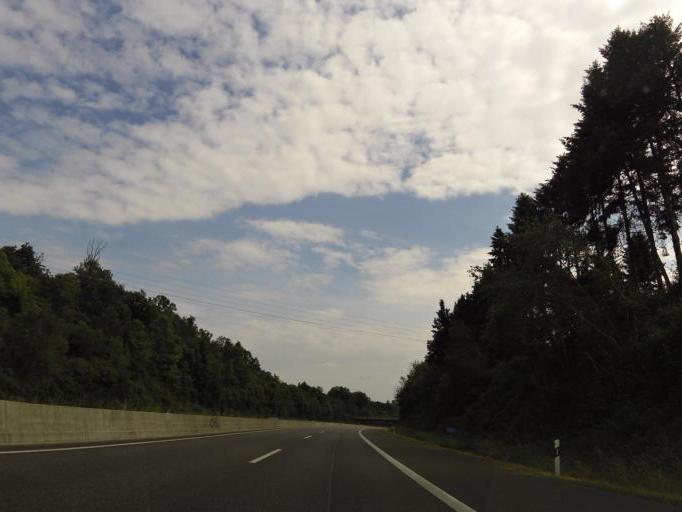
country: DE
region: Hesse
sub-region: Regierungsbezirk Darmstadt
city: Egelsbach
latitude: 49.9828
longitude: 8.6962
